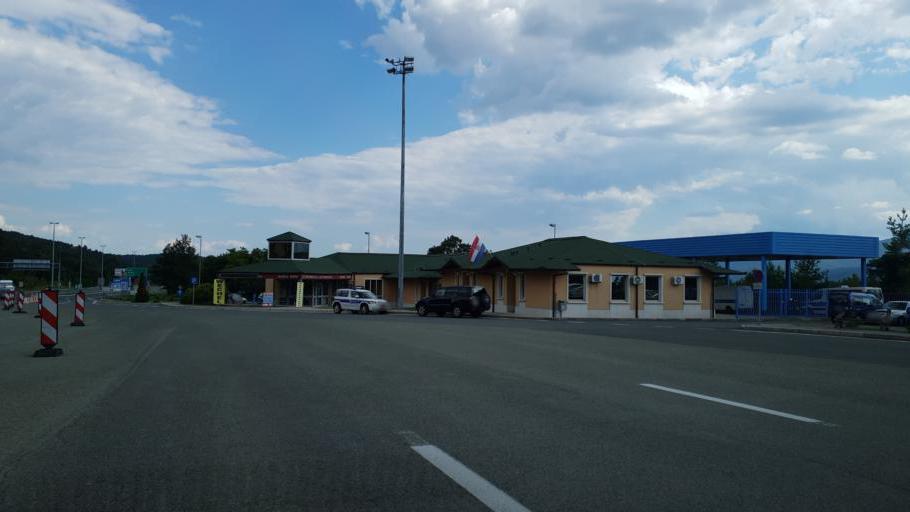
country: SI
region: Ilirska Bistrica
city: Ilirska Bistrica
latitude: 45.4881
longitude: 14.2789
